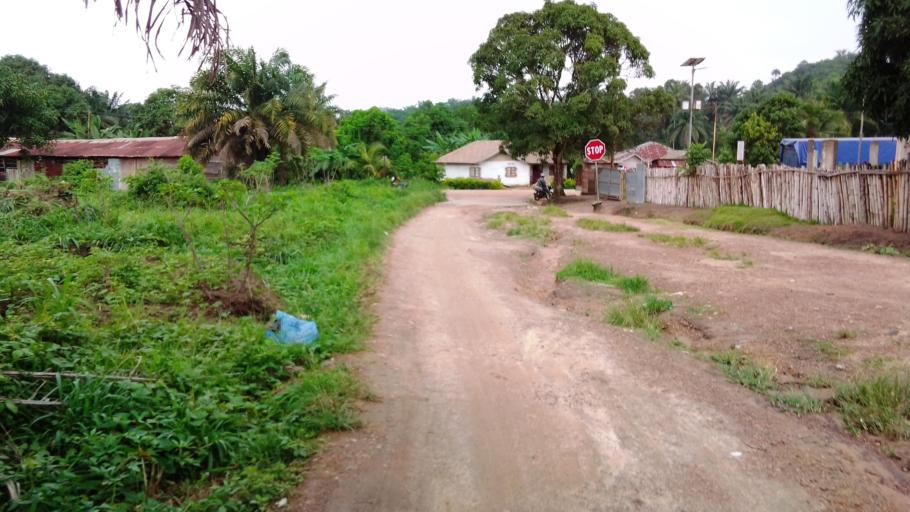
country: SL
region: Eastern Province
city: Kenema
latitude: 7.8770
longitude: -11.1650
